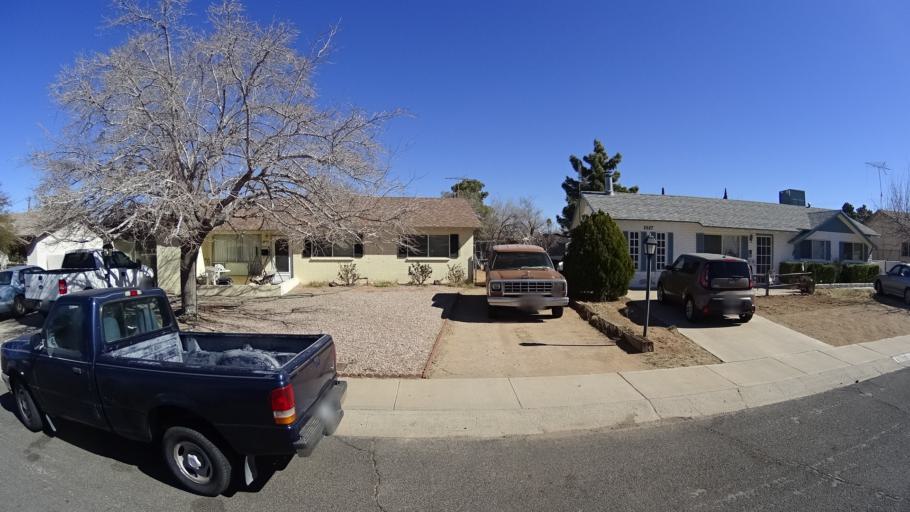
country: US
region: Arizona
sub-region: Mohave County
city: Kingman
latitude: 35.2129
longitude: -114.0191
